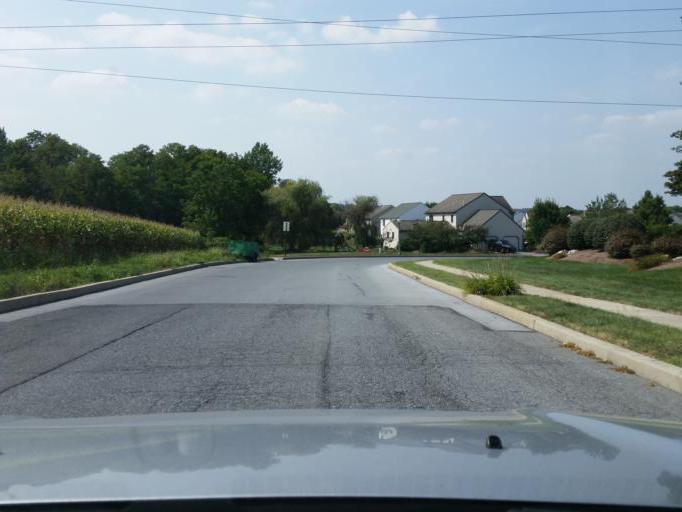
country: US
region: Pennsylvania
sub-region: Dauphin County
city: Hummelstown
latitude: 40.2398
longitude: -76.7160
